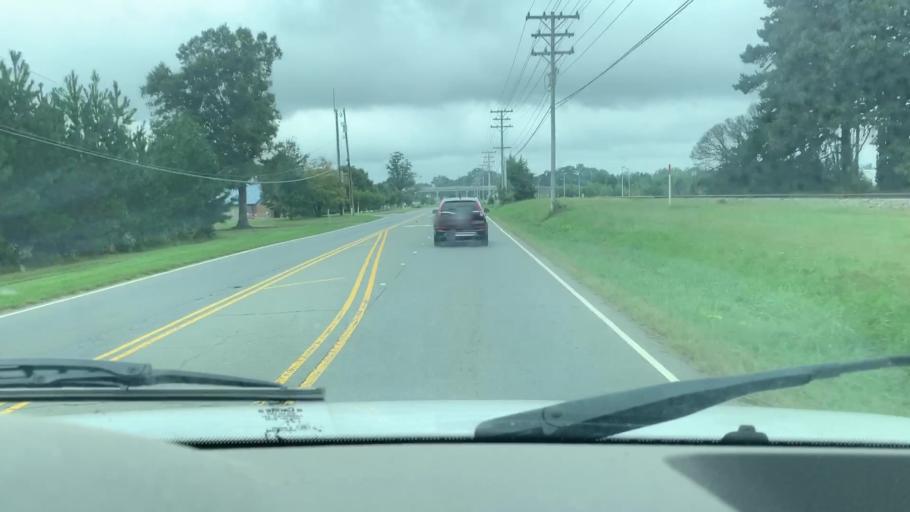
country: US
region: North Carolina
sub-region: Mecklenburg County
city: Huntersville
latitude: 35.3889
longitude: -80.8348
